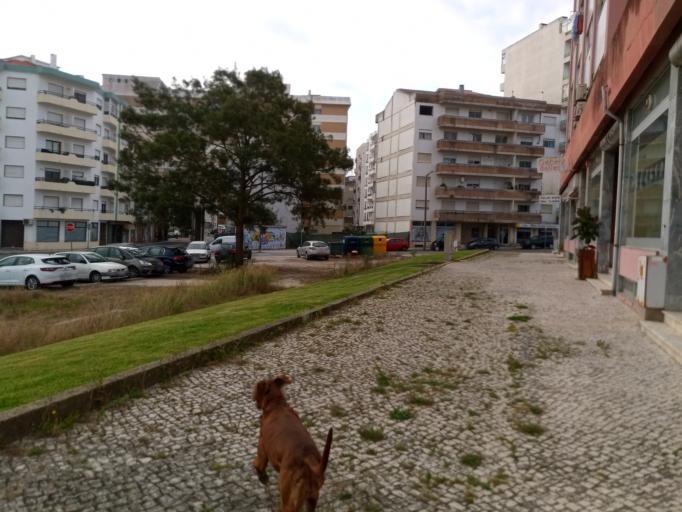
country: PT
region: Leiria
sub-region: Caldas da Rainha
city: Caldas da Rainha
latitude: 39.4112
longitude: -9.1402
